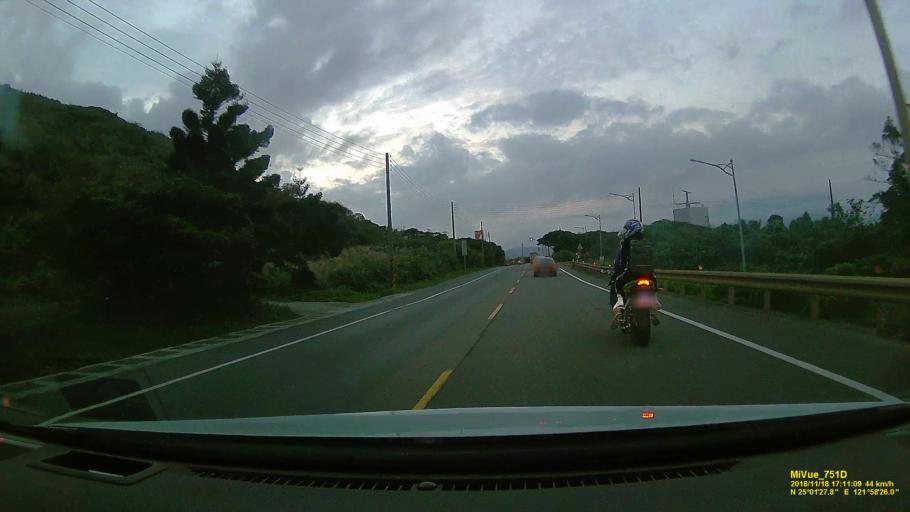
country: TW
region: Taiwan
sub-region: Keelung
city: Keelung
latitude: 25.0244
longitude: 121.9738
